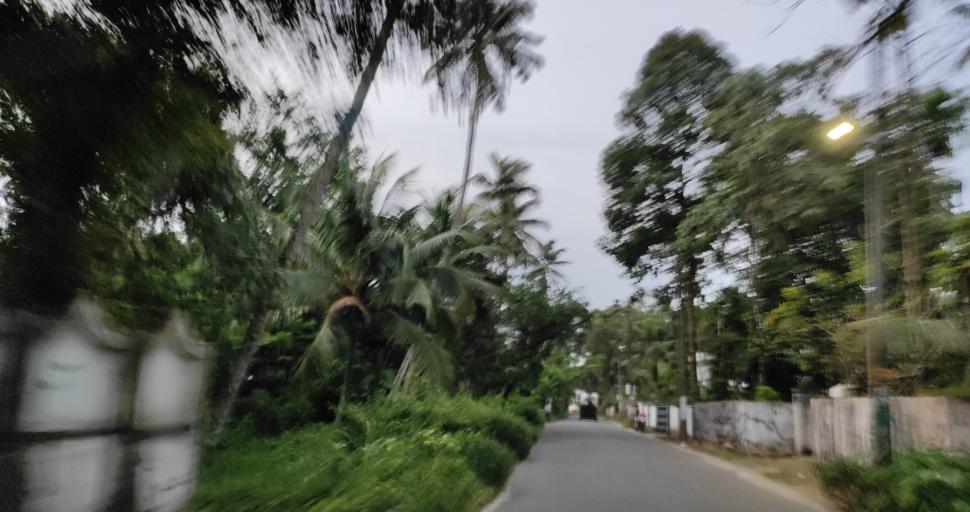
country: IN
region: Kerala
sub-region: Alappuzha
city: Vayalar
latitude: 9.6821
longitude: 76.3184
